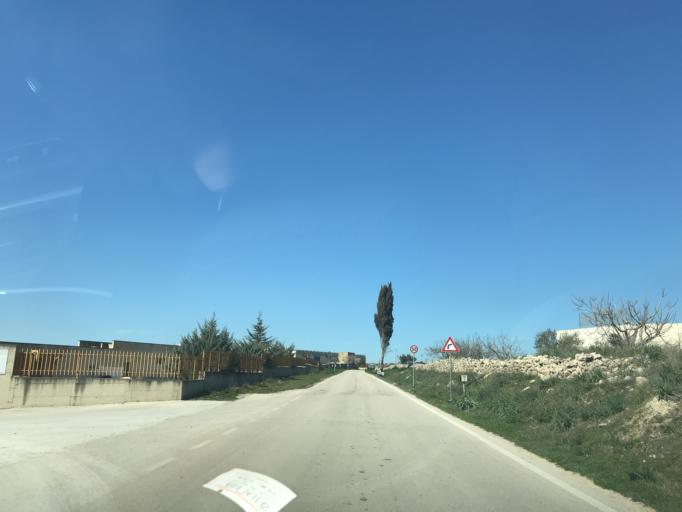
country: IT
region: Apulia
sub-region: Provincia di Bari
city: Gravina in Puglia
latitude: 40.8405
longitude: 16.4276
